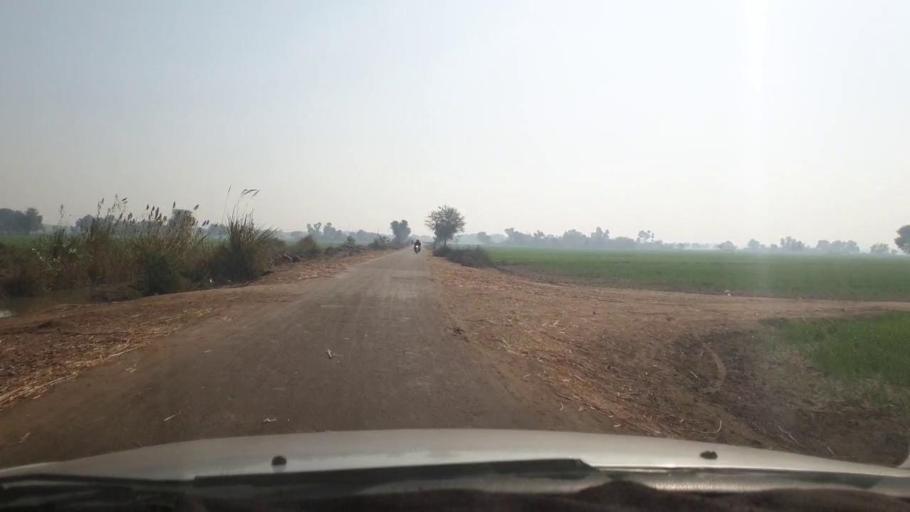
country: PK
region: Sindh
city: Khanpur
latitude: 27.7358
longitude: 69.5102
